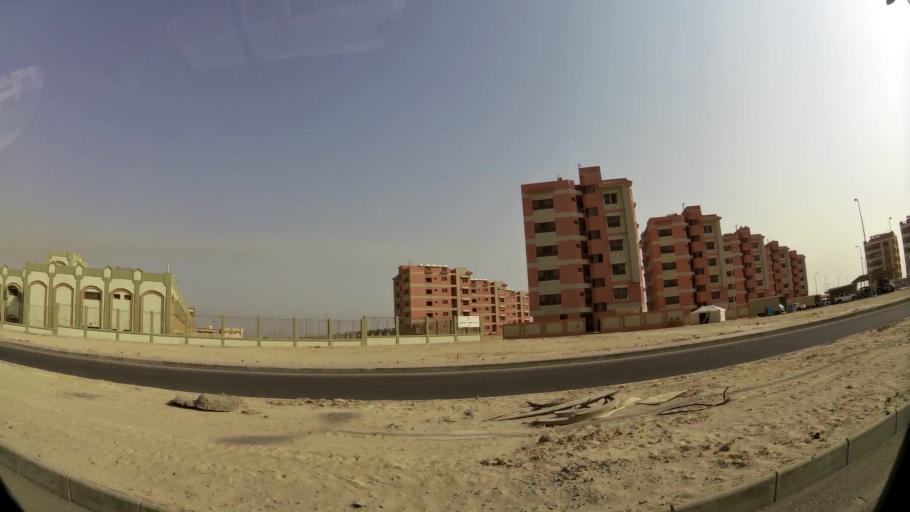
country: KW
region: Al Asimah
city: Ar Rabiyah
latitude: 29.3330
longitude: 47.8125
